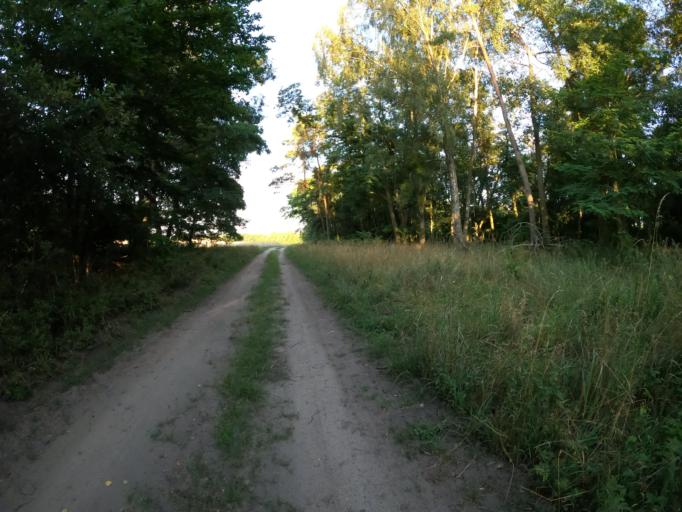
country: DE
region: Brandenburg
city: Althuttendorf
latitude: 53.0261
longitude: 13.8740
